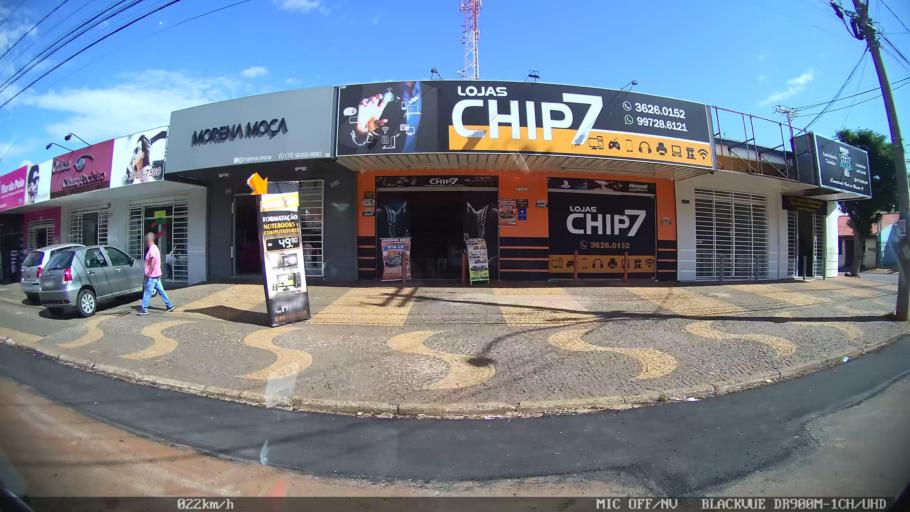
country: BR
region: Sao Paulo
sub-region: Santa Barbara D'Oeste
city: Santa Barbara d'Oeste
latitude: -22.7392
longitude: -47.3794
